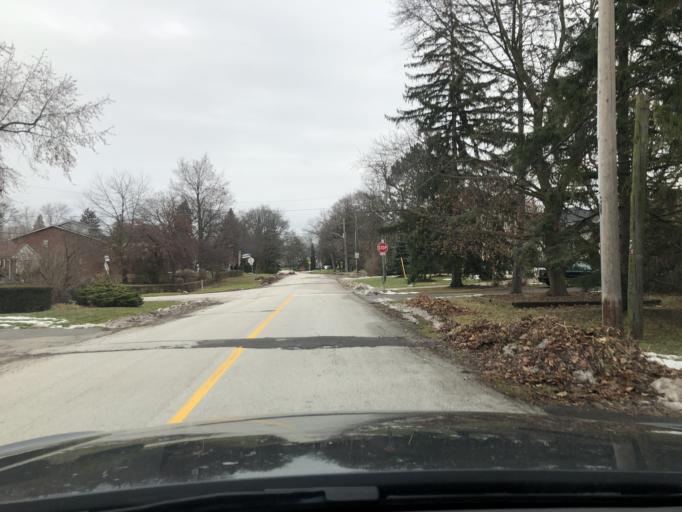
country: CA
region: Ontario
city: Etobicoke
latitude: 43.6950
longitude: -79.5271
